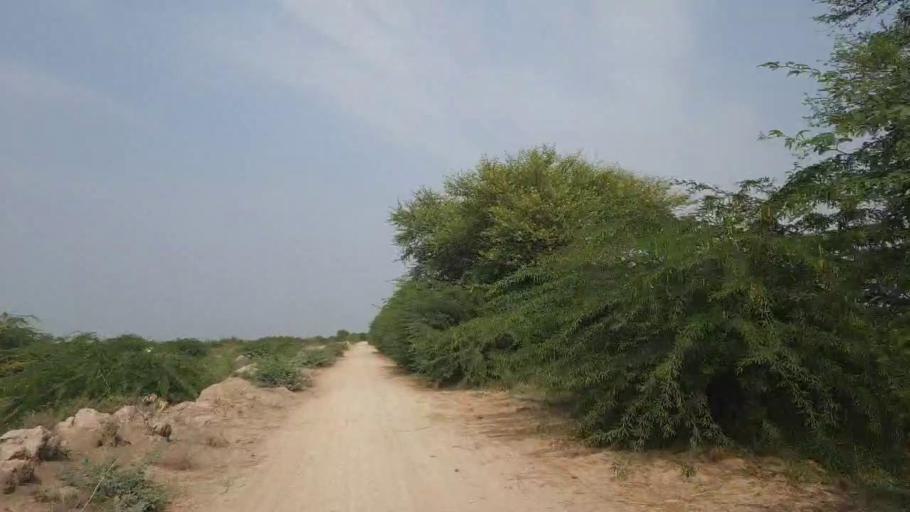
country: PK
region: Sindh
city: Badin
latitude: 24.5620
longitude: 68.7333
